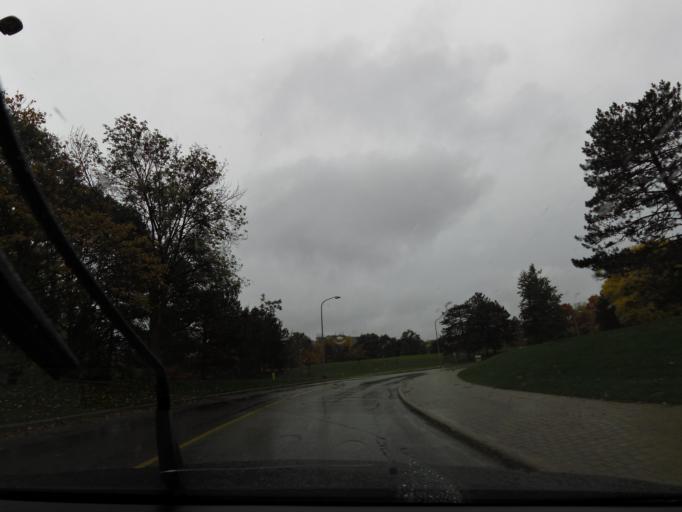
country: CA
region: Ontario
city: Waterloo
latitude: 43.4668
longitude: -80.5410
